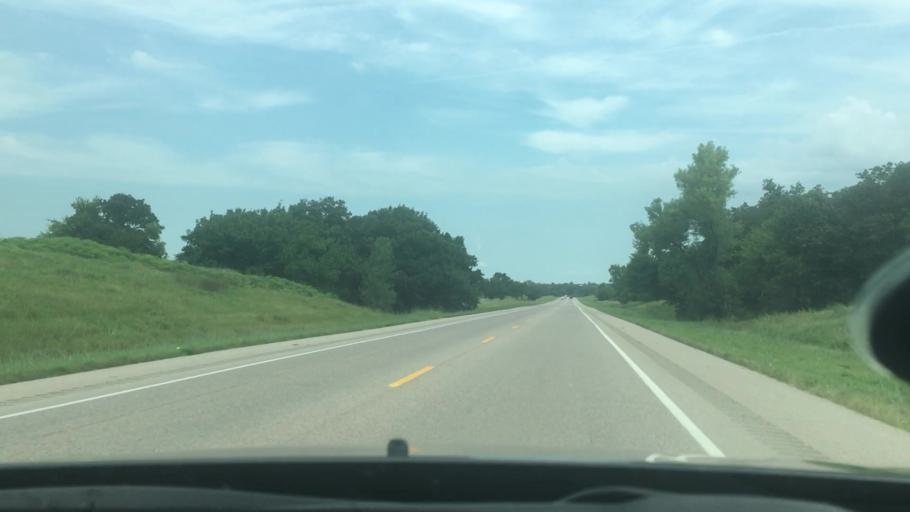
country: US
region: Oklahoma
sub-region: Seminole County
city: Seminole
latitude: 35.1636
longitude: -96.6743
